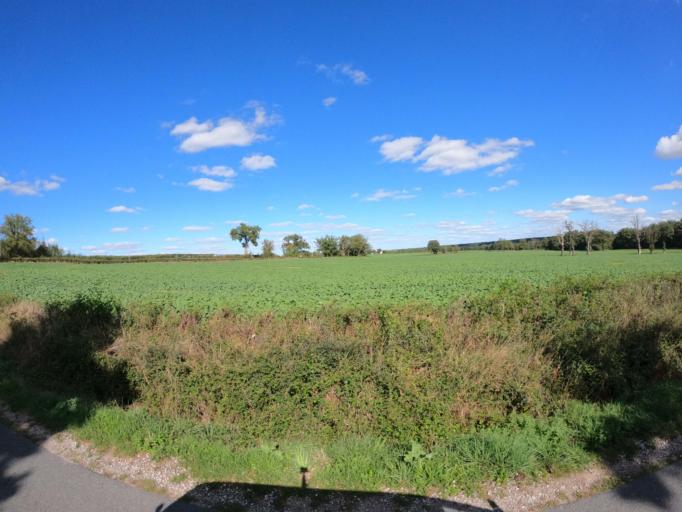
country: FR
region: Auvergne
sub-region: Departement de l'Allier
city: Doyet
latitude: 46.3966
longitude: 2.7515
